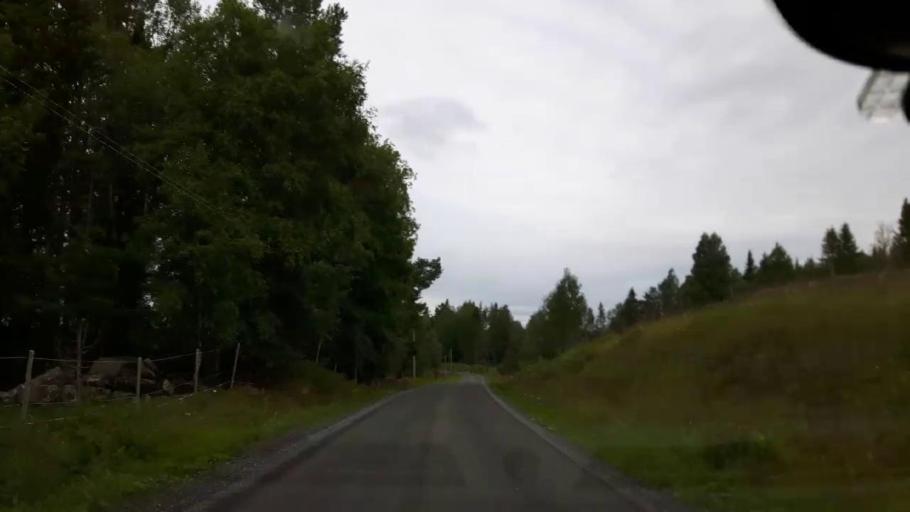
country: SE
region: Jaemtland
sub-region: Krokoms Kommun
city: Krokom
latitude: 63.2709
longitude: 14.4048
